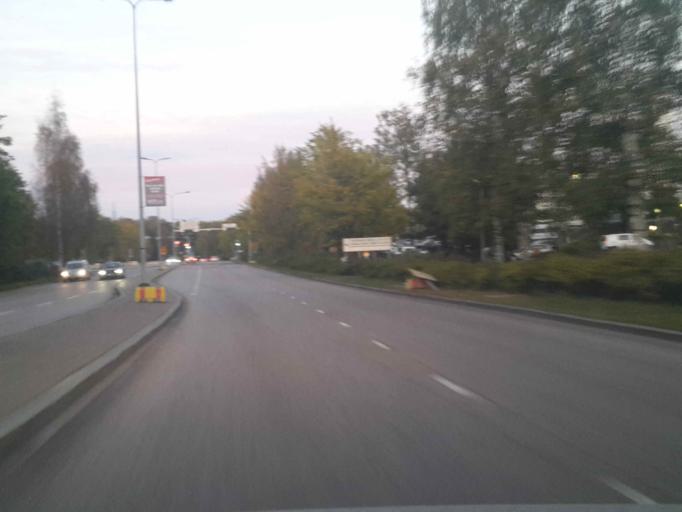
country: FI
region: Uusimaa
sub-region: Helsinki
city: Koukkuniemi
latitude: 60.1713
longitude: 24.7767
